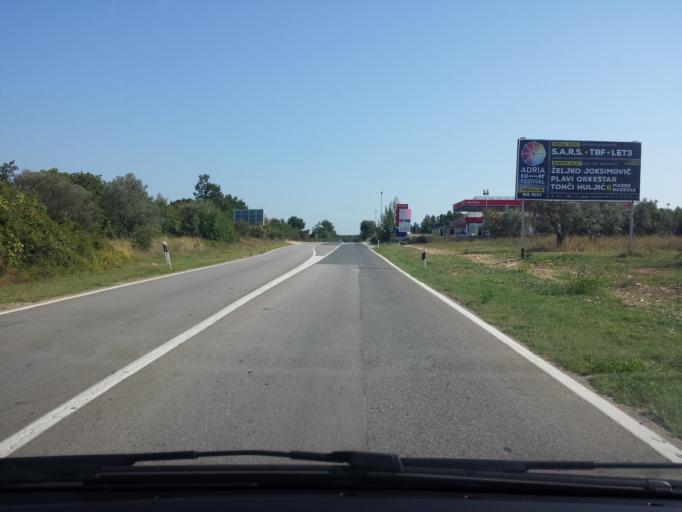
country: HR
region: Istarska
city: Galizana
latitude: 44.9143
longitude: 13.8495
